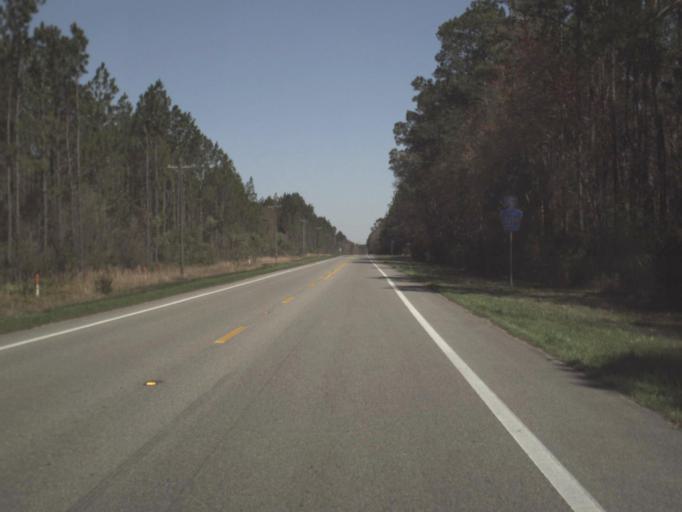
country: US
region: Florida
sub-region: Gadsden County
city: Gretna
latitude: 30.3869
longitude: -84.7075
